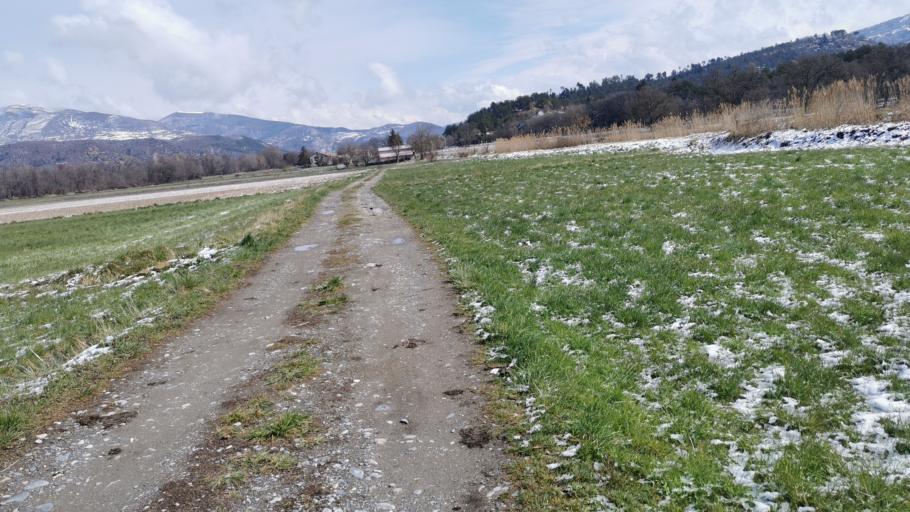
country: FR
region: Provence-Alpes-Cote d'Azur
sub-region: Departement des Alpes-de-Haute-Provence
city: Mallemoisson
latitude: 44.0572
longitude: 6.1719
